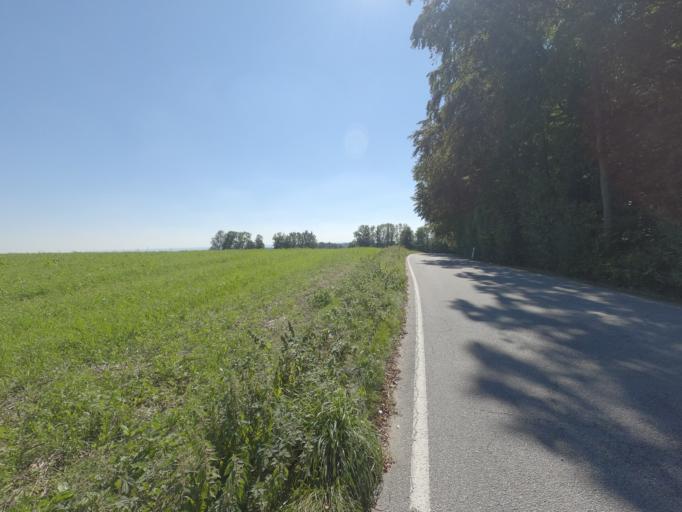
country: DE
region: Bavaria
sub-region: Lower Bavaria
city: Deggendorf
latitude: 48.8268
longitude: 12.9996
